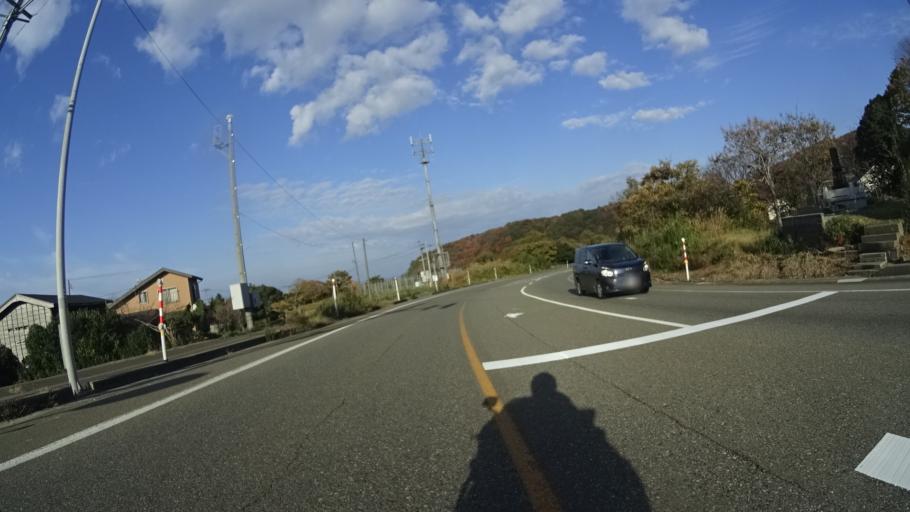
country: JP
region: Niigata
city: Kashiwazaki
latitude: 37.3288
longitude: 138.4559
